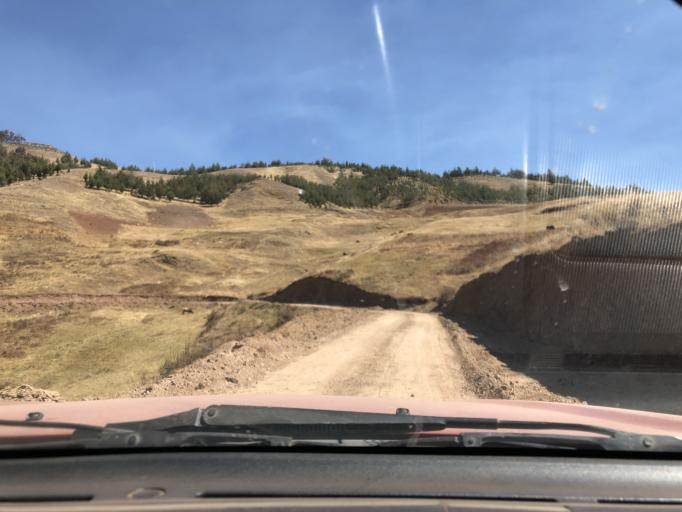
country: PE
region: Ayacucho
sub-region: Provincia de La Mar
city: Chilcas
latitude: -13.1804
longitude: -73.8449
